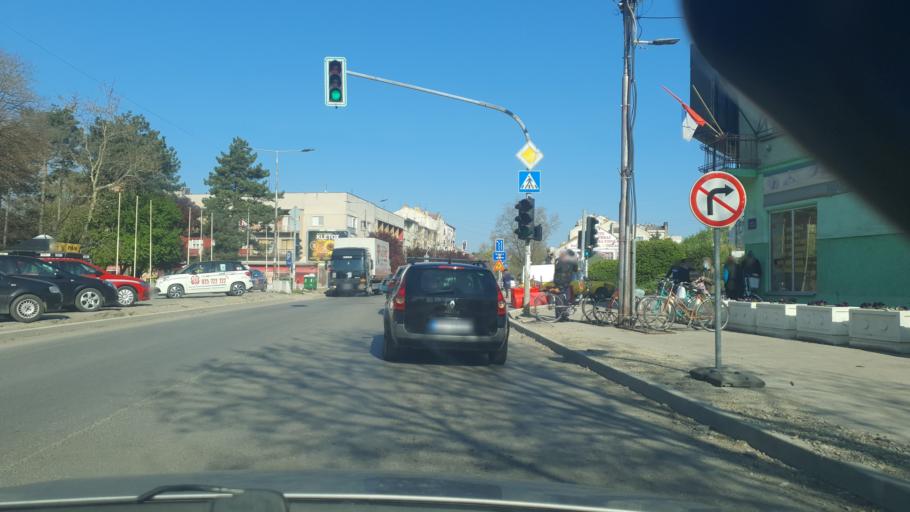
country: RS
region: Autonomna Pokrajina Vojvodina
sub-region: Zapadnobacki Okrug
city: Kula
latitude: 45.6092
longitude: 19.5335
